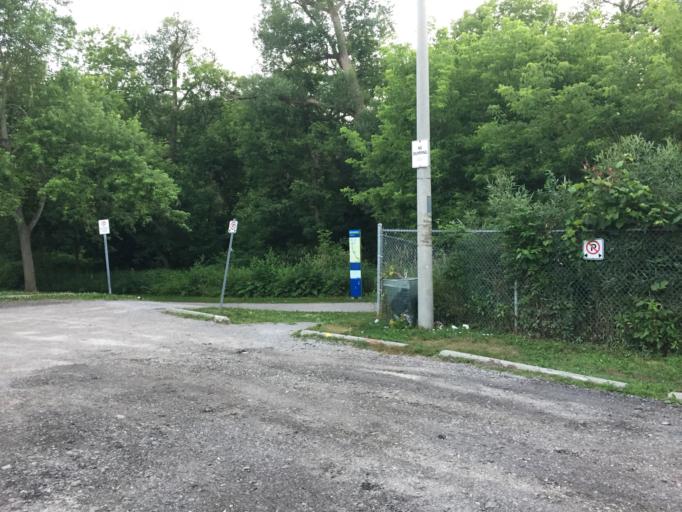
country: CA
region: Ontario
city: Oshawa
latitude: 43.8688
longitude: -78.8461
